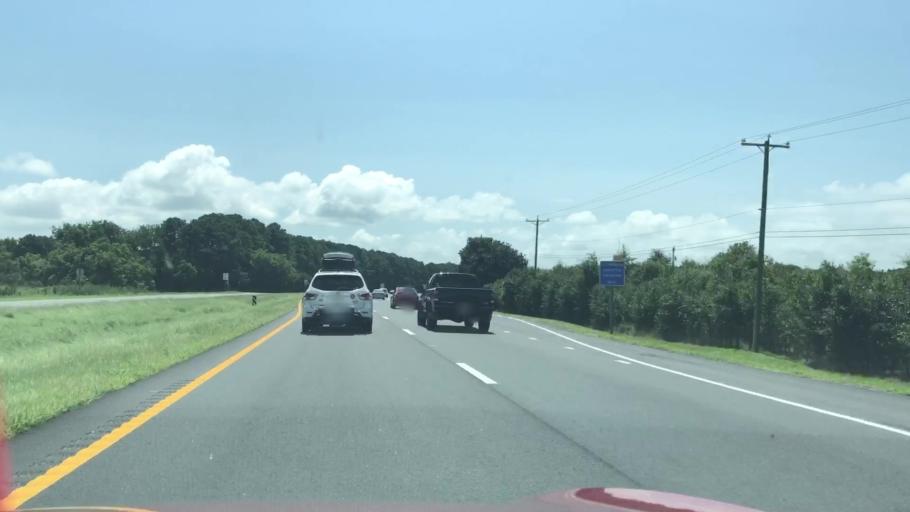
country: US
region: Virginia
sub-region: Northampton County
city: Cape Charles
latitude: 37.1402
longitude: -75.9677
